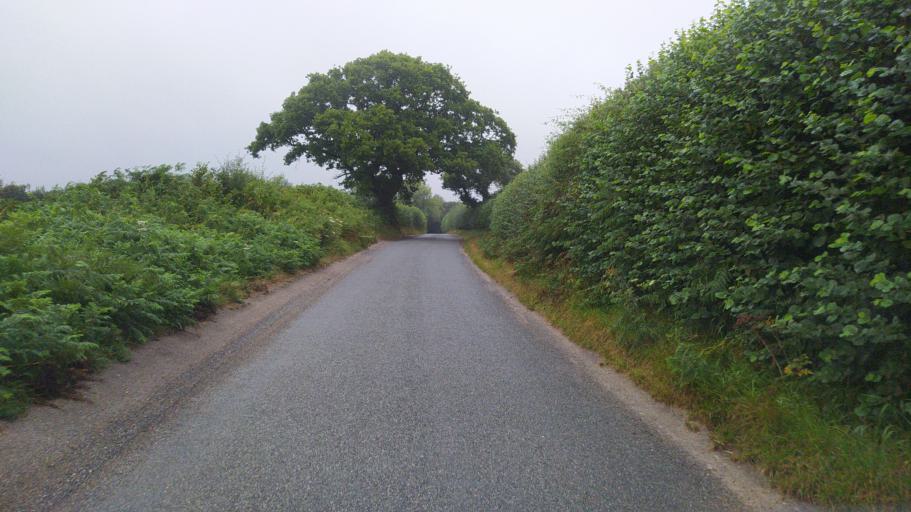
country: GB
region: England
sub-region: Wiltshire
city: Ansty
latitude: 51.0042
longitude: -2.1142
